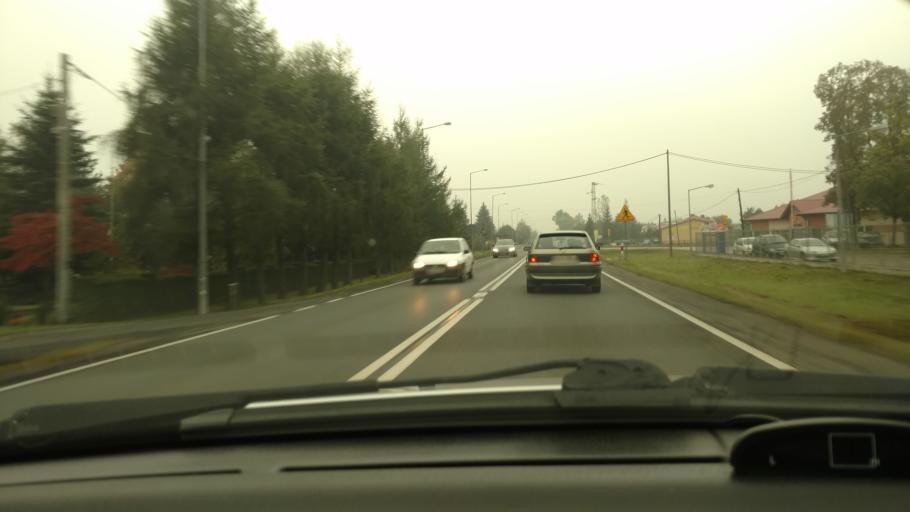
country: PL
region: Lesser Poland Voivodeship
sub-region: Powiat gorlicki
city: Kobylanka
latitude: 49.7002
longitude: 21.2145
